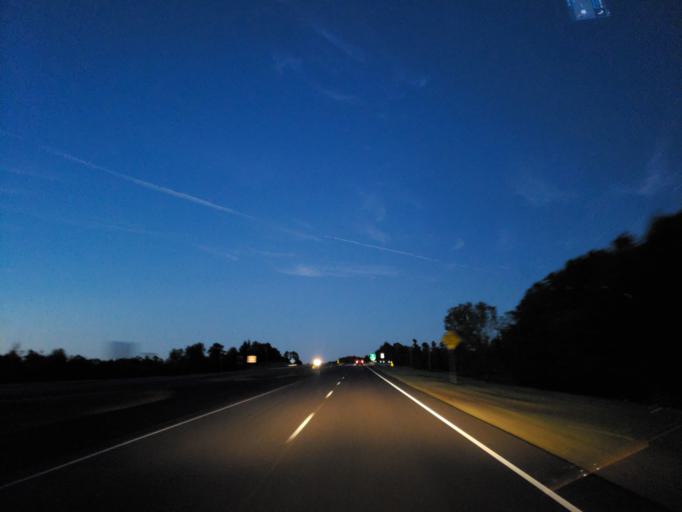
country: US
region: Mississippi
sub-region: Clarke County
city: Quitman
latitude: 32.0380
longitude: -88.6791
